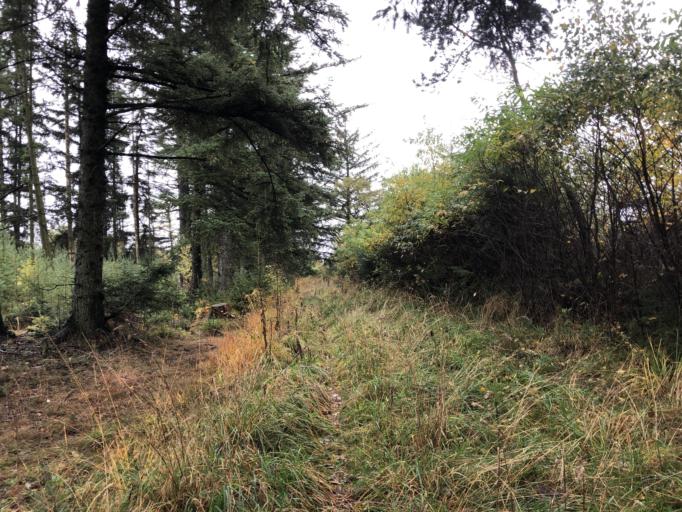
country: DK
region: Central Jutland
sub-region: Holstebro Kommune
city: Ulfborg
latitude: 56.2668
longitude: 8.4345
